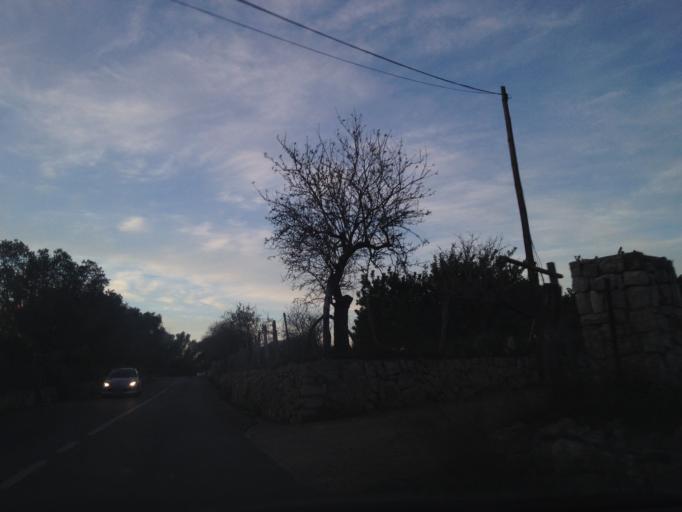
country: ES
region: Balearic Islands
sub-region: Illes Balears
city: Pollenca
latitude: 39.8629
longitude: 3.0456
